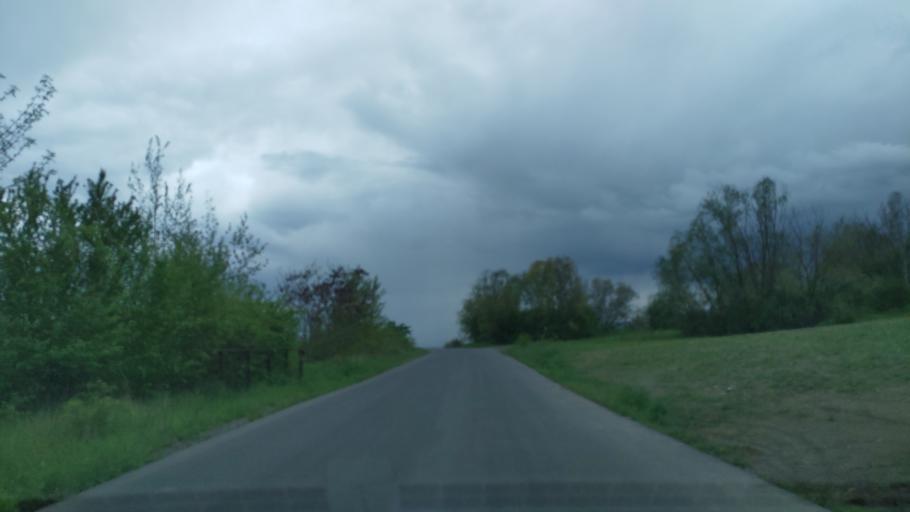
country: CZ
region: Ustecky
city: Trmice
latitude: 50.6468
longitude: 13.9768
